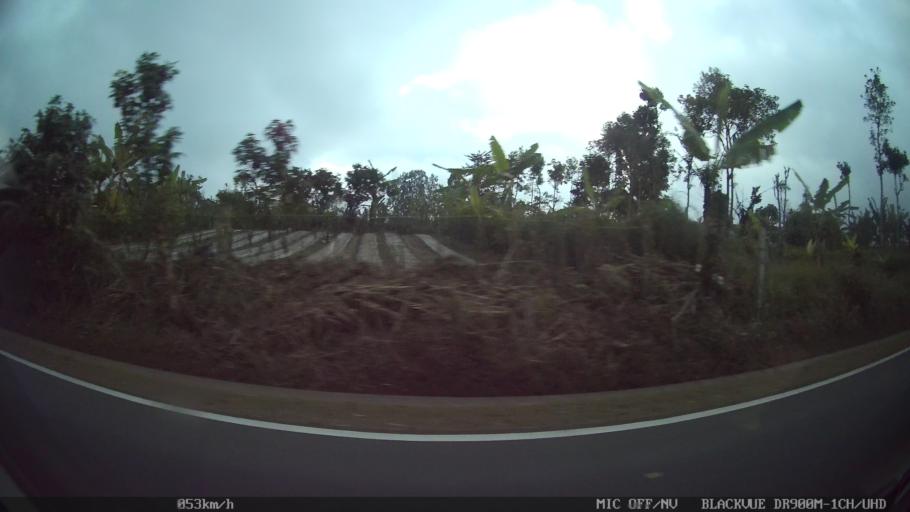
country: ID
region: Bali
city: Banjar Kedisan
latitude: -8.2791
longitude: 115.3233
